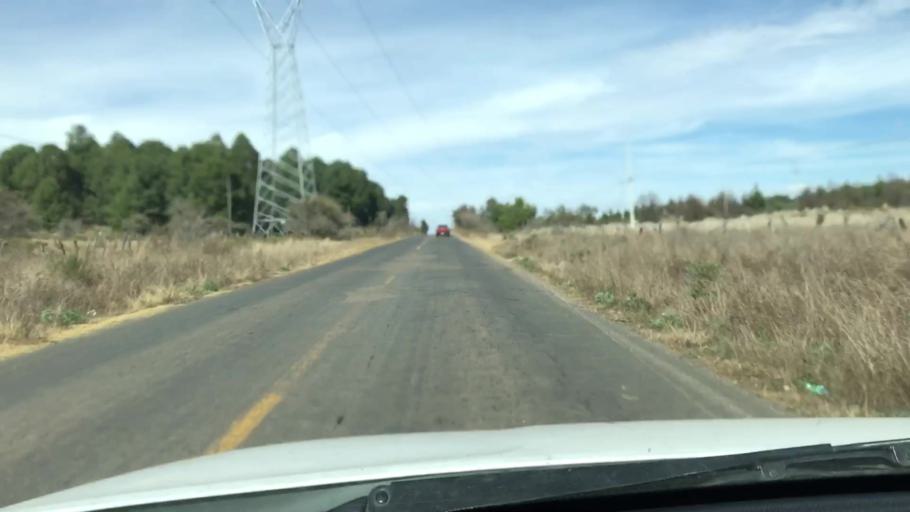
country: MX
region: Jalisco
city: Chiquilistlan
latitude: 20.1041
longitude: -103.7182
